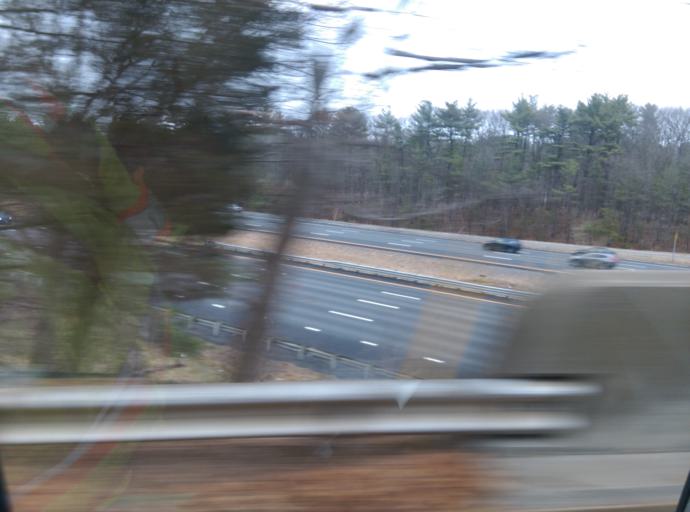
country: US
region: New Hampshire
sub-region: Rockingham County
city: Seabrook
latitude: 42.8742
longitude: -70.8873
